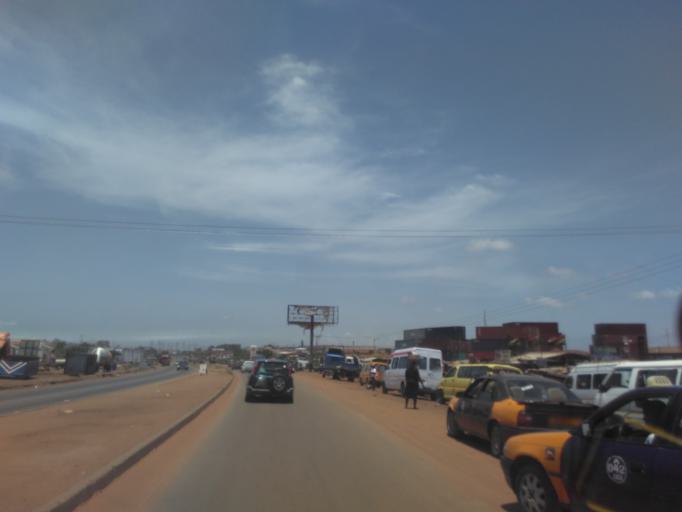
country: GH
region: Greater Accra
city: Tema
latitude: 5.6859
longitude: -0.0132
